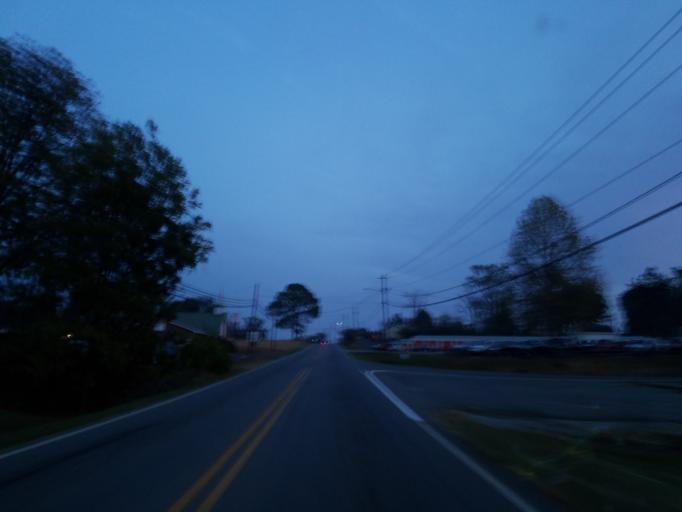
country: US
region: Georgia
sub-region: Pickens County
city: Jasper
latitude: 34.4727
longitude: -84.4368
